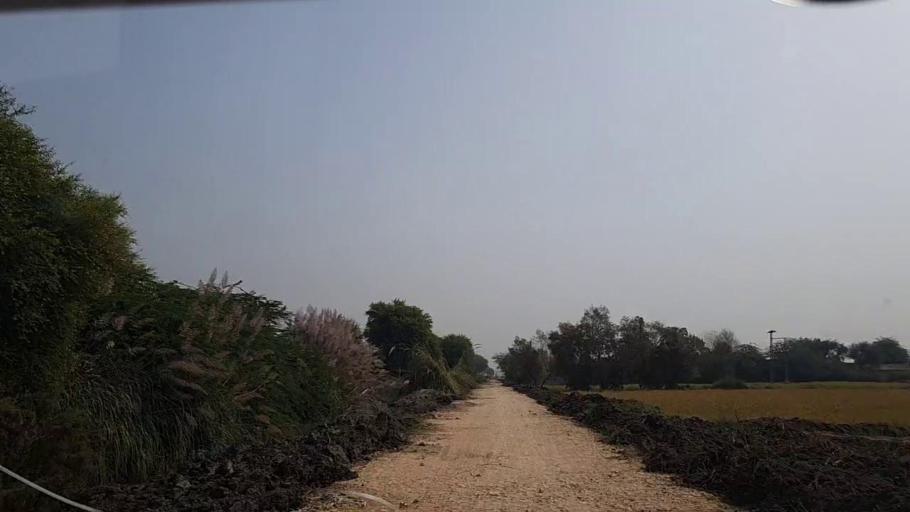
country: PK
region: Sindh
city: Shikarpur
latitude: 27.9199
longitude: 68.5817
